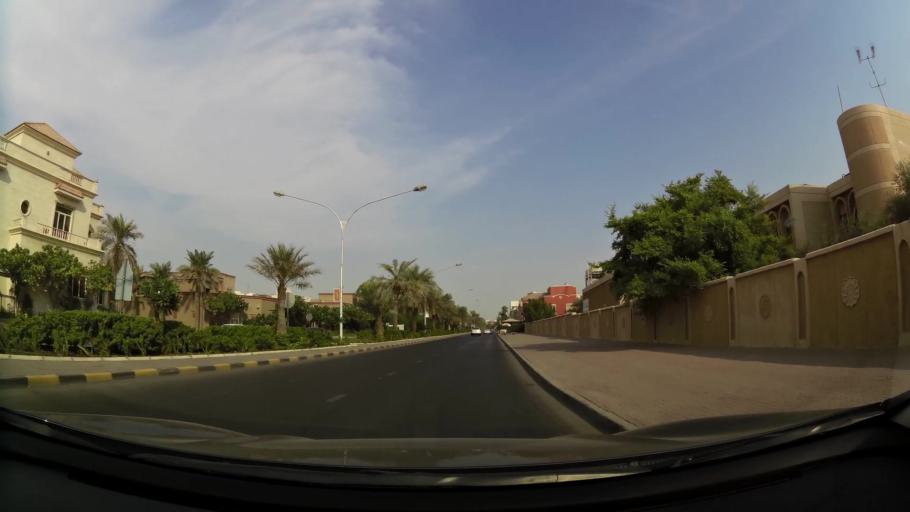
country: KW
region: Al Asimah
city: Ash Shamiyah
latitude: 29.3147
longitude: 47.9890
